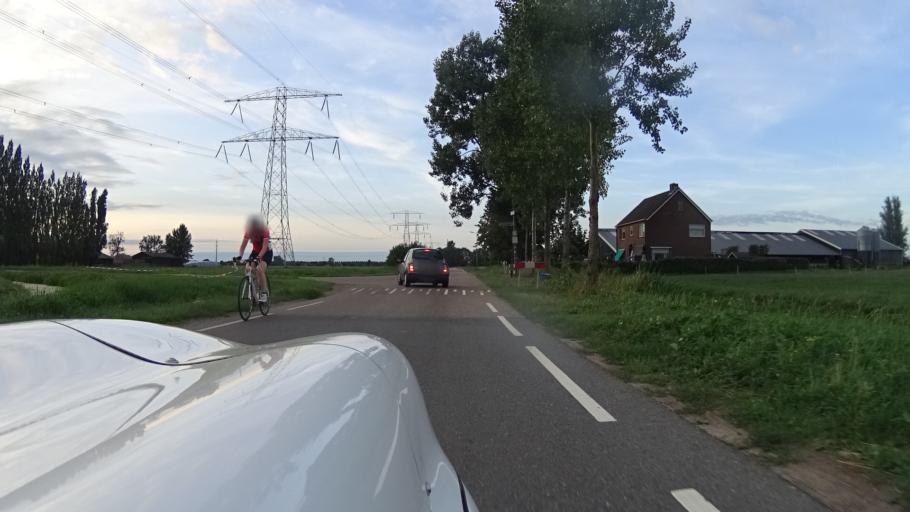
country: NL
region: South Holland
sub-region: Gemeente Sliedrecht
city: Sliedrecht
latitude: 51.8327
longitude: 4.8042
